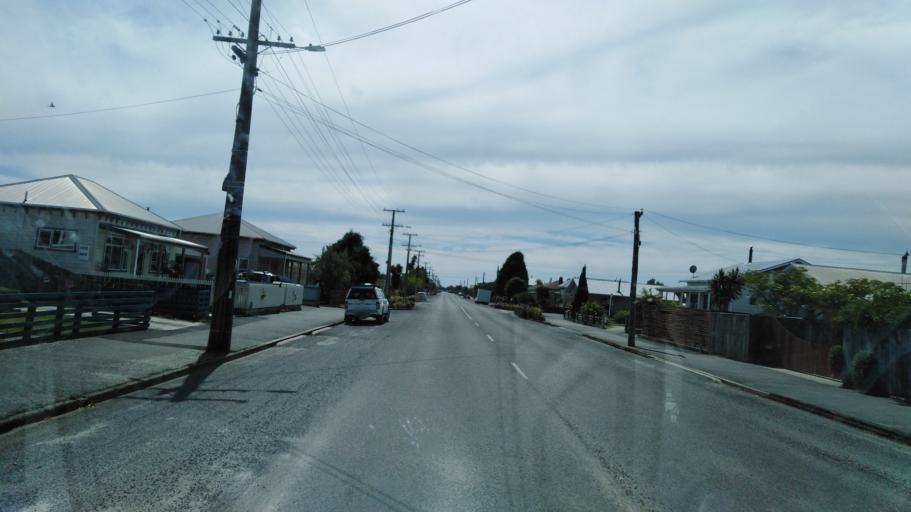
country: NZ
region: West Coast
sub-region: Buller District
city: Westport
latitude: -41.7536
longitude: 171.6054
